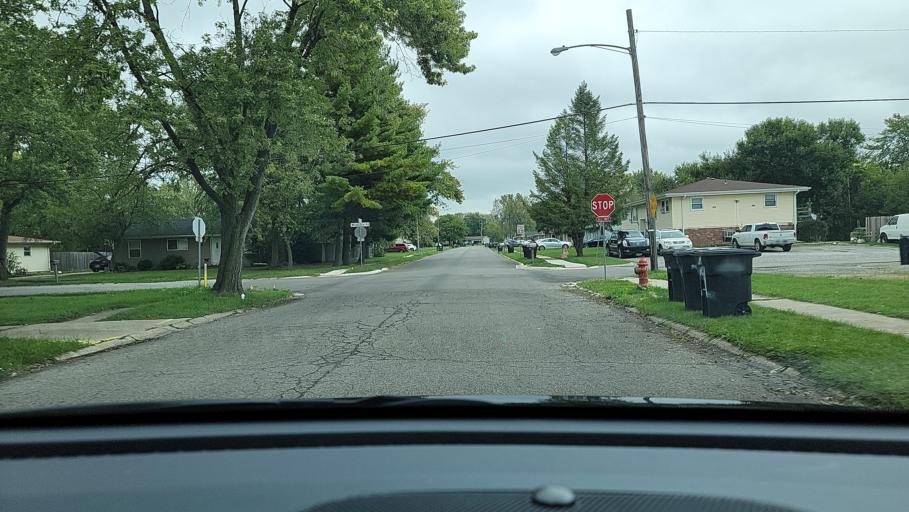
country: US
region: Indiana
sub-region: Porter County
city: Portage
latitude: 41.5568
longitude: -87.2006
